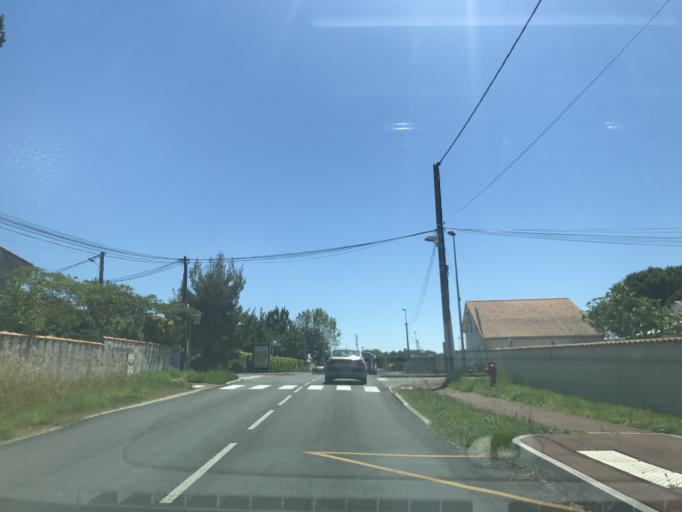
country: FR
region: Poitou-Charentes
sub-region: Departement de la Charente-Maritime
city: Meschers-sur-Gironde
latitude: 45.5756
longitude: -0.9606
